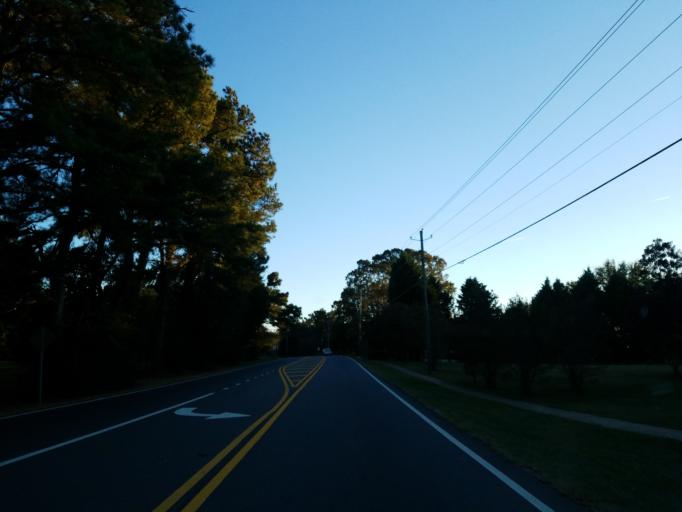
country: US
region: Georgia
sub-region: Forsyth County
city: Cumming
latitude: 34.2183
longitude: -84.1347
